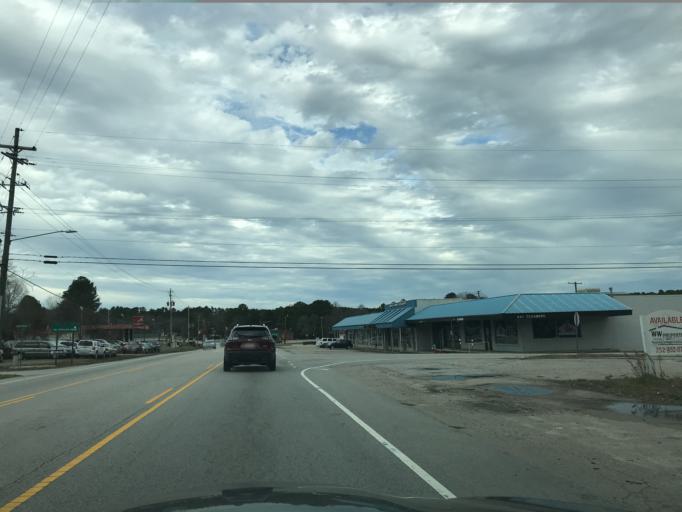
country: US
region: North Carolina
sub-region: Franklin County
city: Louisburg
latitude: 36.1041
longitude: -78.2927
